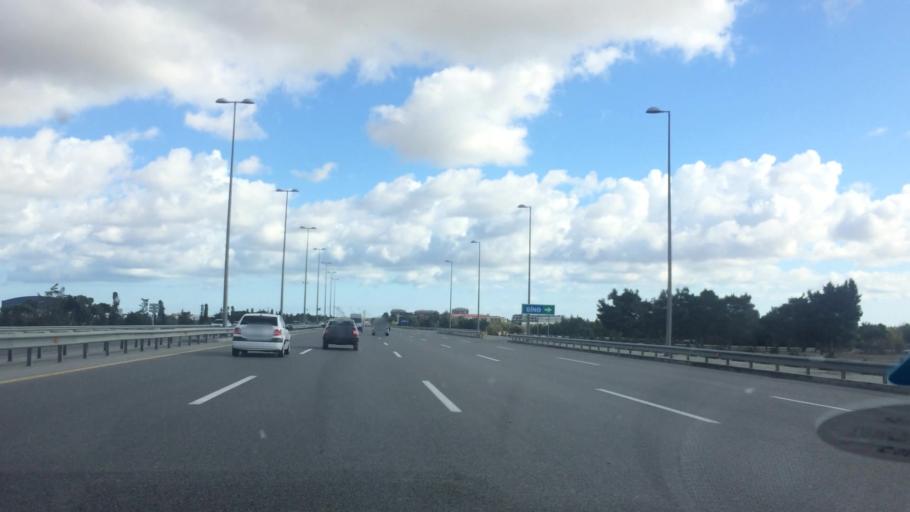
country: AZ
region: Baki
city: Biny Selo
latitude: 40.4498
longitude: 50.0588
